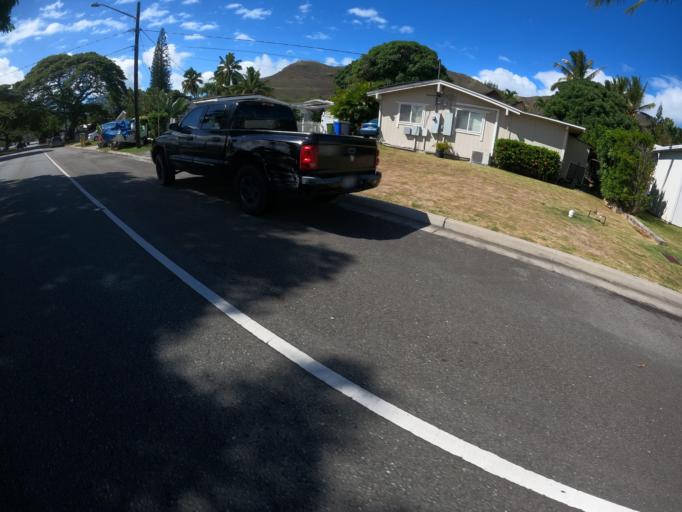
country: US
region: Hawaii
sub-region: Honolulu County
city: Kailua
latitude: 21.4122
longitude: -157.7531
